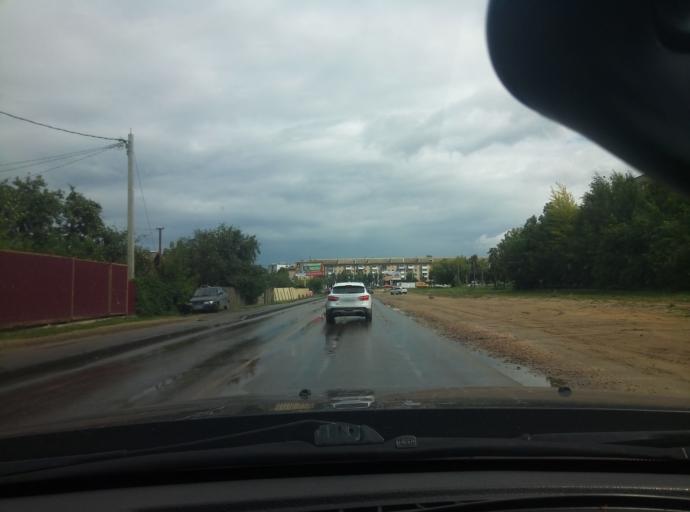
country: RU
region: Tula
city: Novomoskovsk
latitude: 54.0185
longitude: 38.2922
